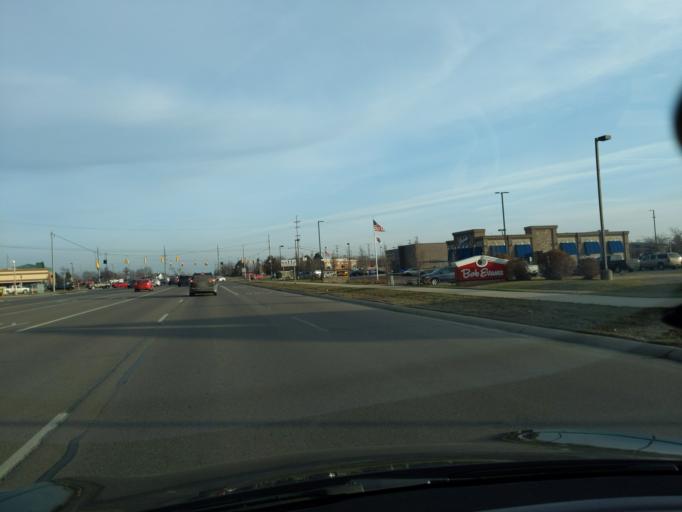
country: US
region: Michigan
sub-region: Livingston County
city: Howell
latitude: 42.5874
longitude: -83.8760
